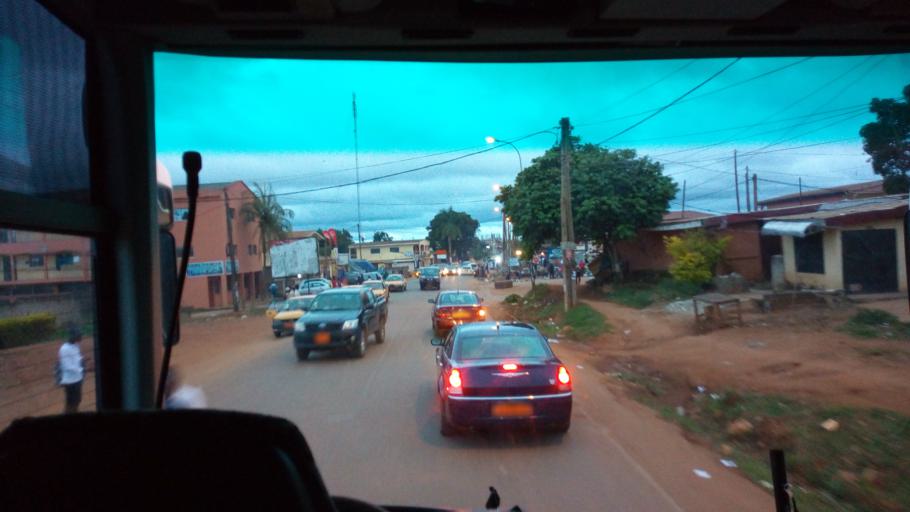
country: CM
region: Centre
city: Yaounde
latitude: 3.7895
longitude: 11.5237
